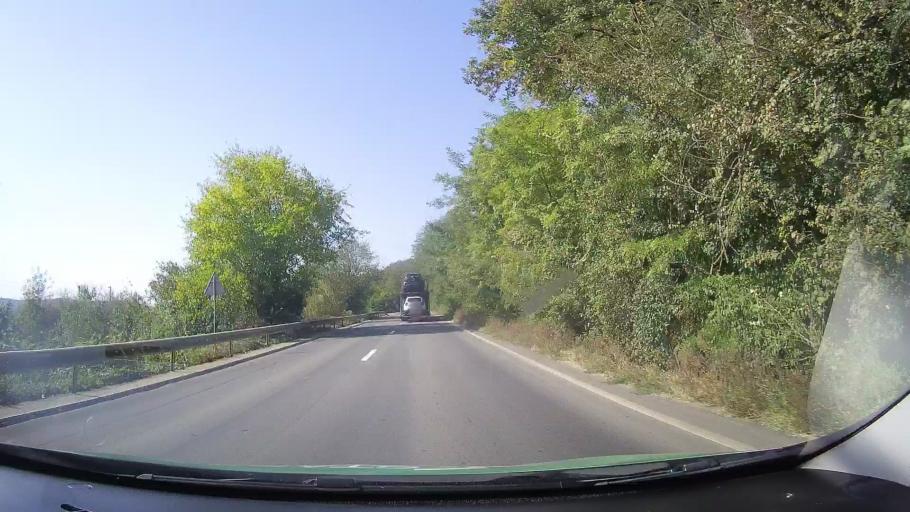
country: RO
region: Arad
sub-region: Comuna Conop
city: Conop
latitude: 46.0980
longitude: 21.9066
